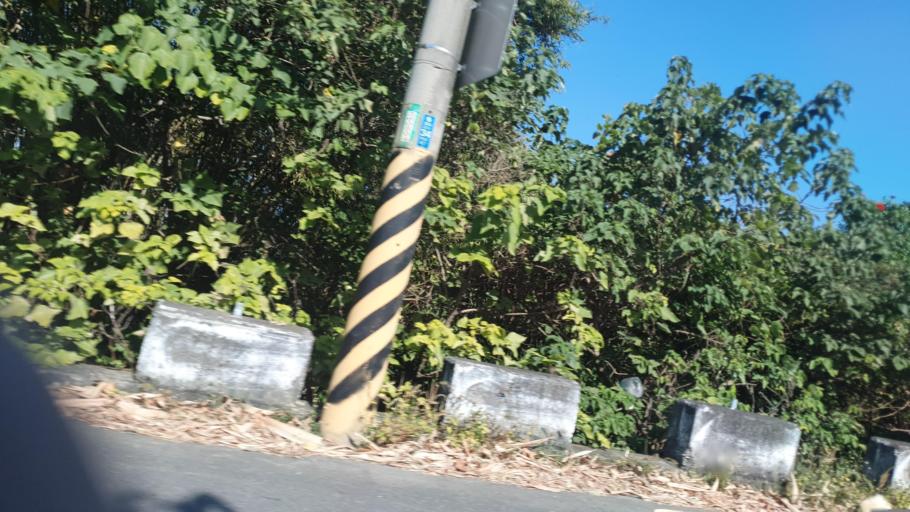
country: TW
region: Taiwan
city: Yujing
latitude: 23.0397
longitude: 120.3584
